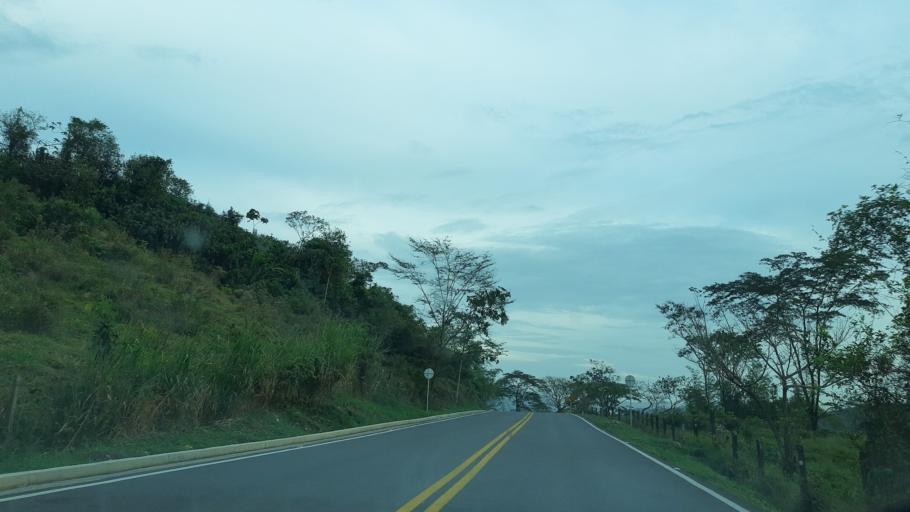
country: CO
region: Casanare
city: Sabanalarga
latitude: 4.7809
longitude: -73.0506
